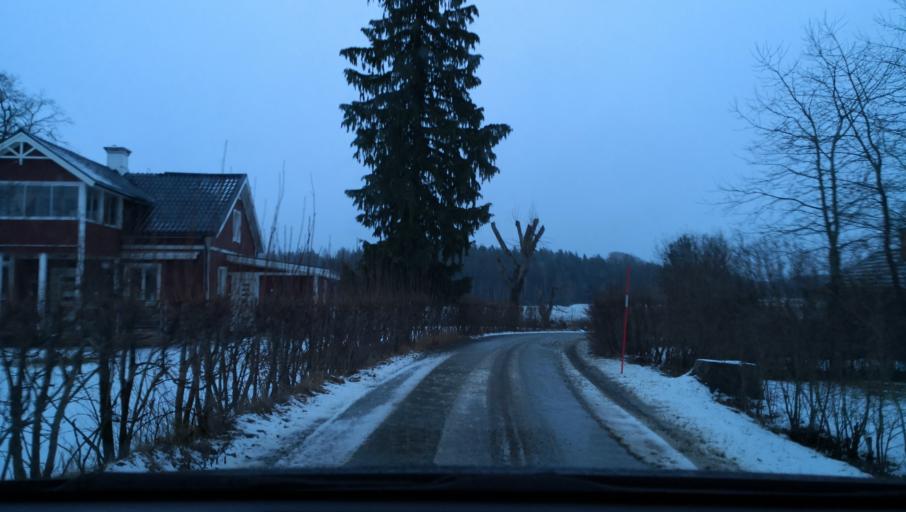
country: SE
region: Vaestmanland
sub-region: Kungsors Kommun
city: Kungsoer
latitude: 59.4015
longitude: 16.2041
